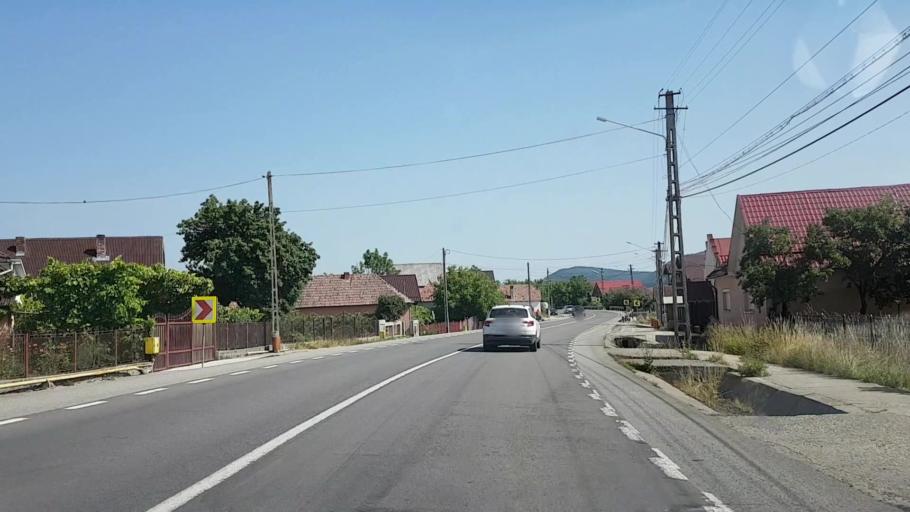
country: RO
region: Bistrita-Nasaud
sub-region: Comuna Sieu-Magherus
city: Sieu-Magherus
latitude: 47.0959
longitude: 24.3682
